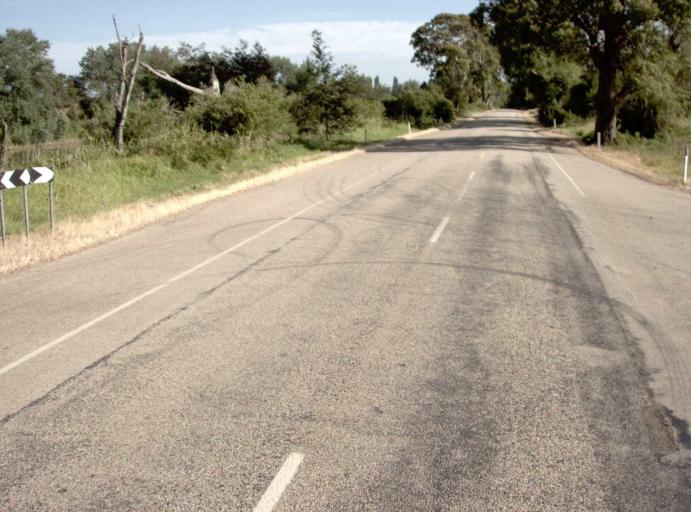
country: AU
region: Victoria
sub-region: East Gippsland
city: Lakes Entrance
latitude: -37.8284
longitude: 147.8631
